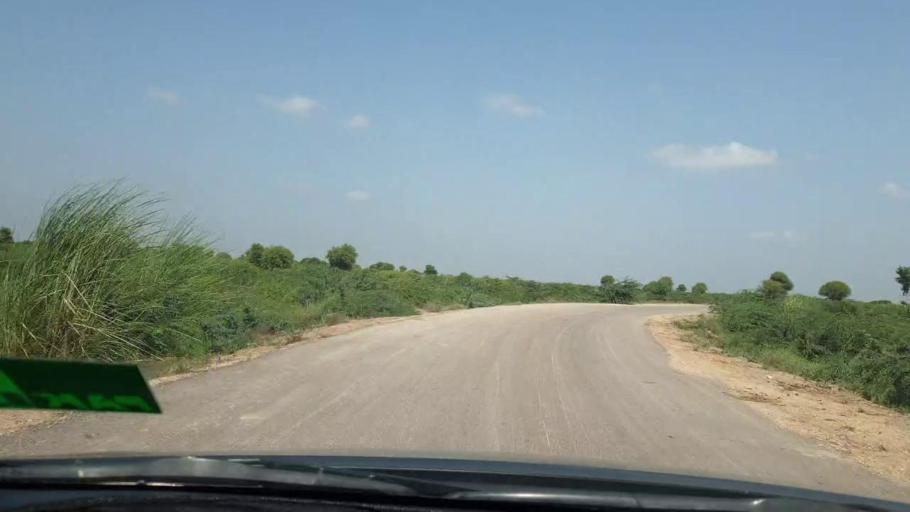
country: PK
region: Sindh
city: Digri
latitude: 24.9959
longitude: 69.1217
